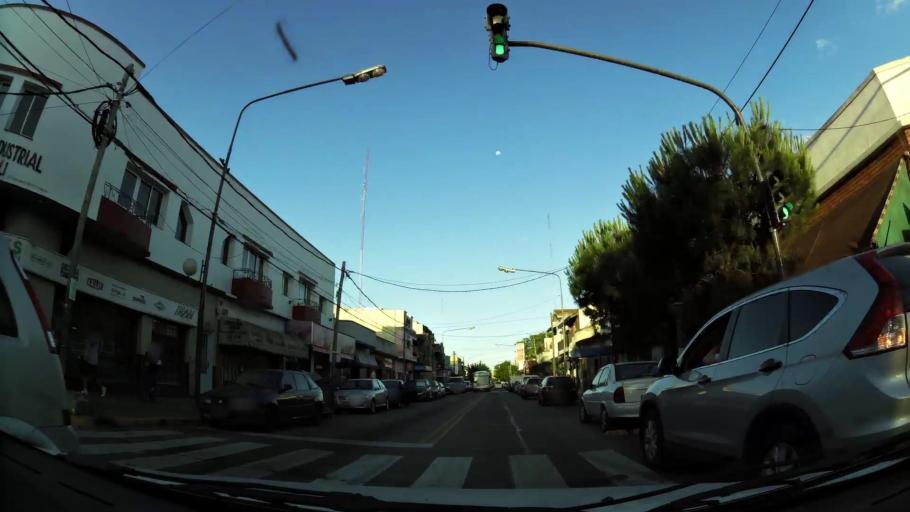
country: AR
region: Buenos Aires
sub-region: Partido de General San Martin
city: General San Martin
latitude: -34.5486
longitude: -58.5055
